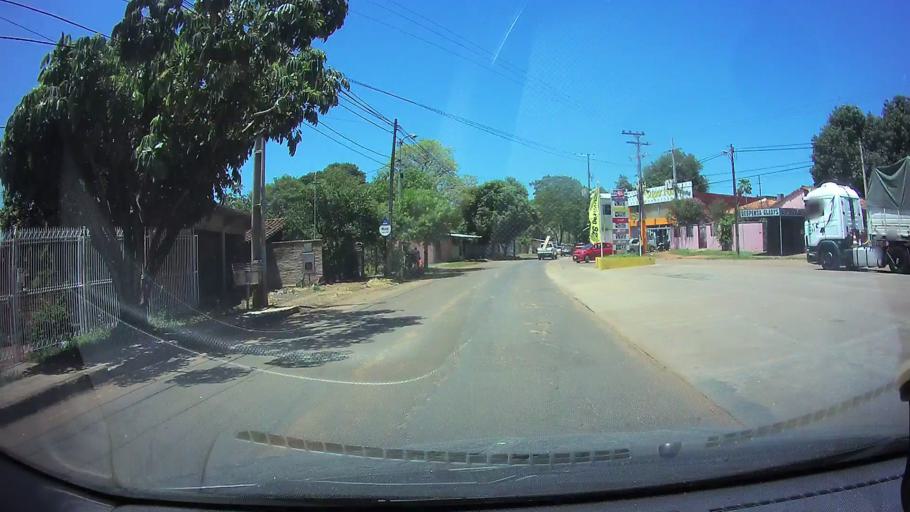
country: PY
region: Central
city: San Lorenzo
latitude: -25.3361
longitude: -57.4854
